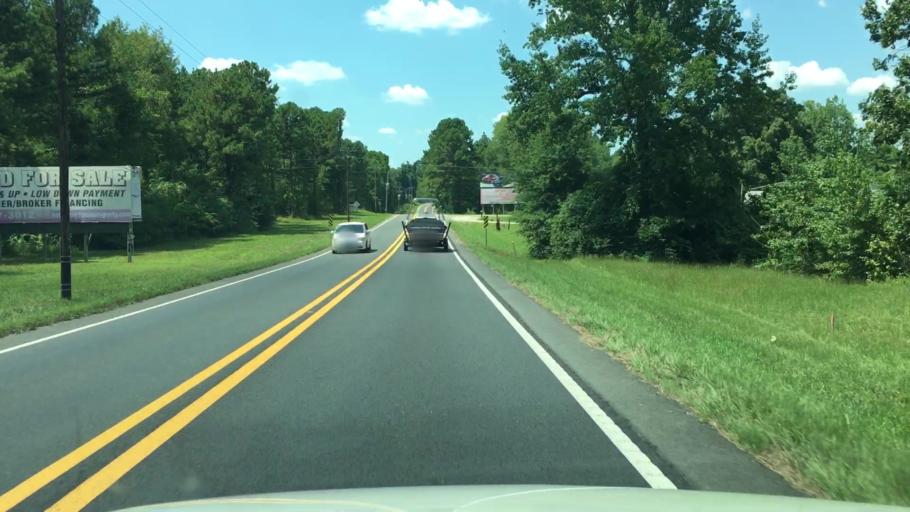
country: US
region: Arkansas
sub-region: Garland County
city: Lake Hamilton
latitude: 34.2694
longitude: -93.1449
